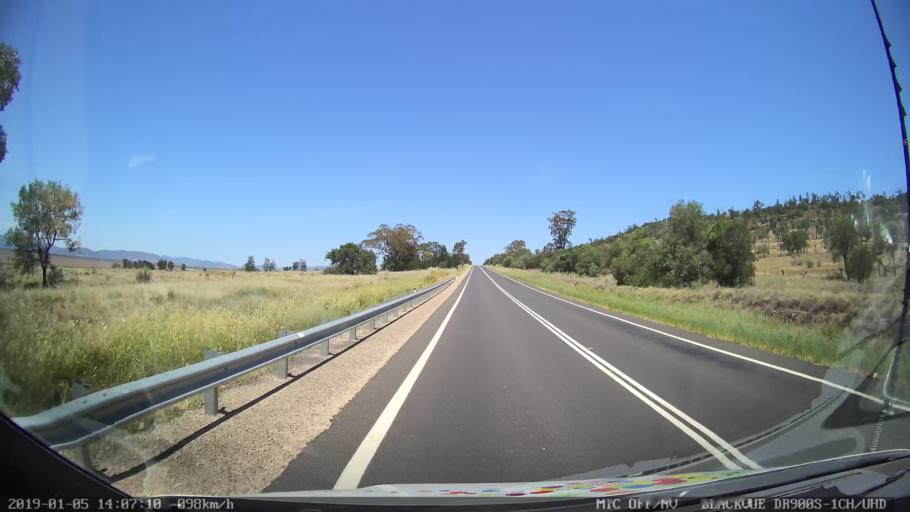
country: AU
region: New South Wales
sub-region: Gunnedah
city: Gunnedah
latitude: -31.2201
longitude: 150.4029
